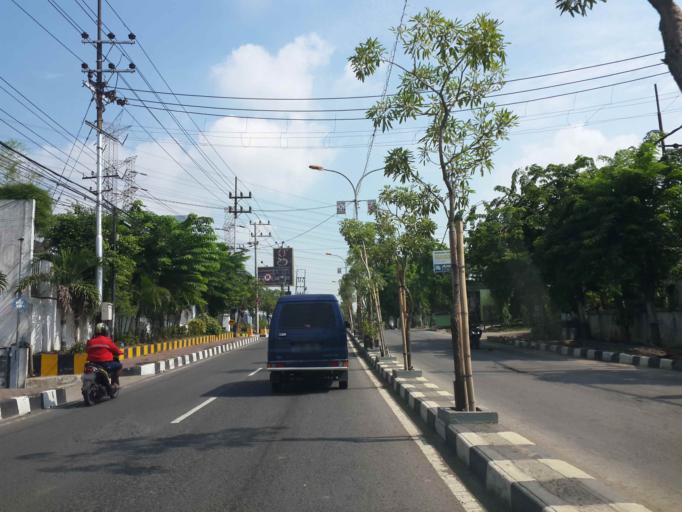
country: ID
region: East Java
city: Kebomas
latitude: -7.1862
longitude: 112.6477
